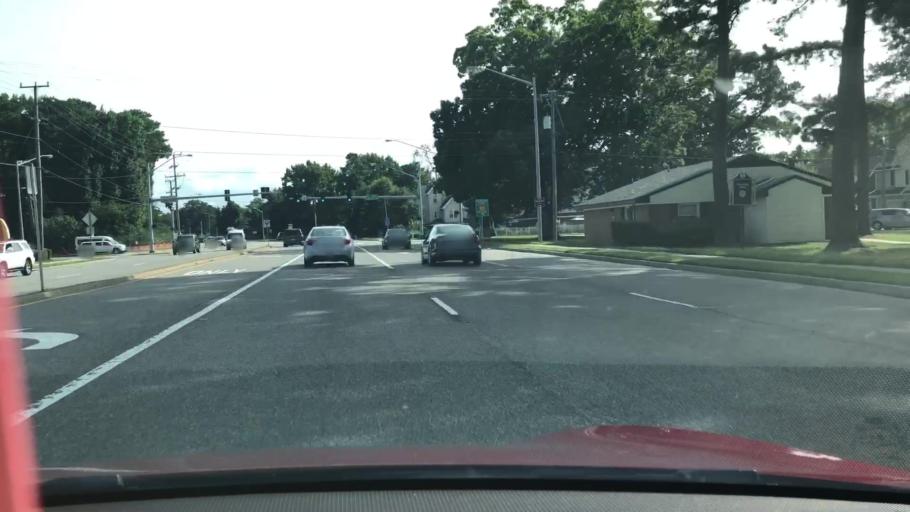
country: US
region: Virginia
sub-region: City of Virginia Beach
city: Virginia Beach
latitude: 36.8453
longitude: -75.9955
